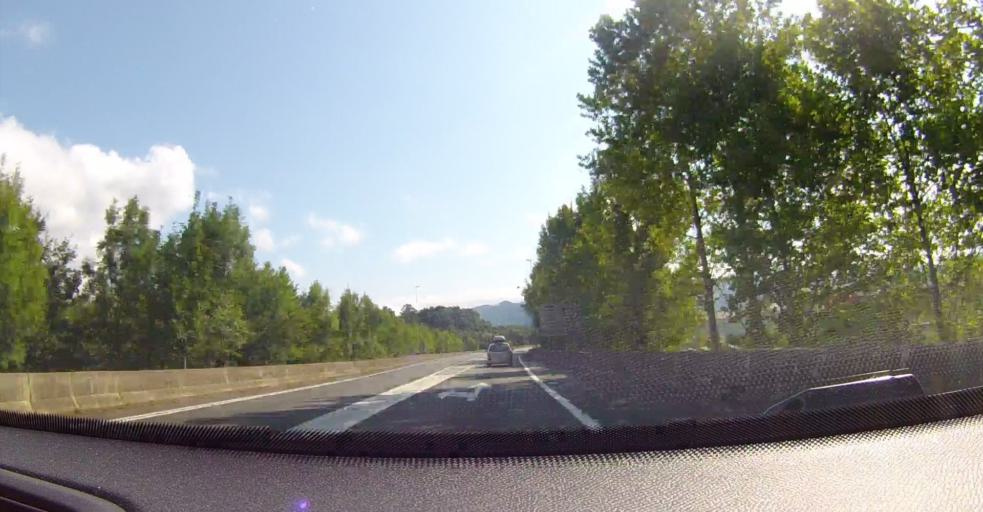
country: ES
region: Basque Country
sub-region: Bizkaia
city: Gernika-Lumo
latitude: 43.3065
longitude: -2.6754
